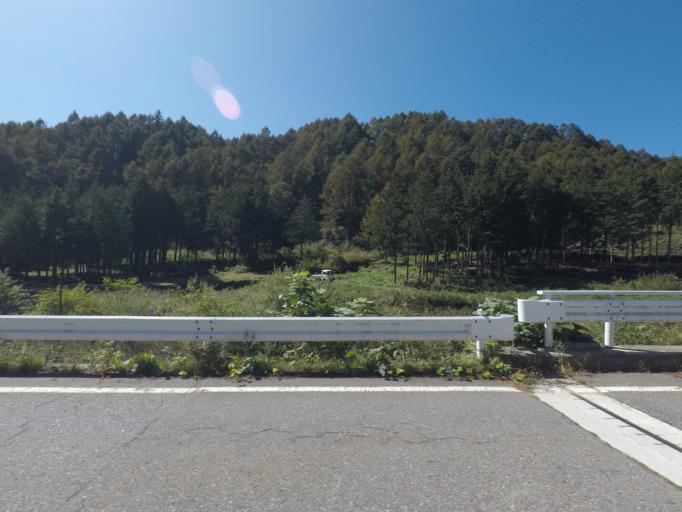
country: JP
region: Nagano
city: Shiojiri
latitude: 35.9876
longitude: 137.7412
